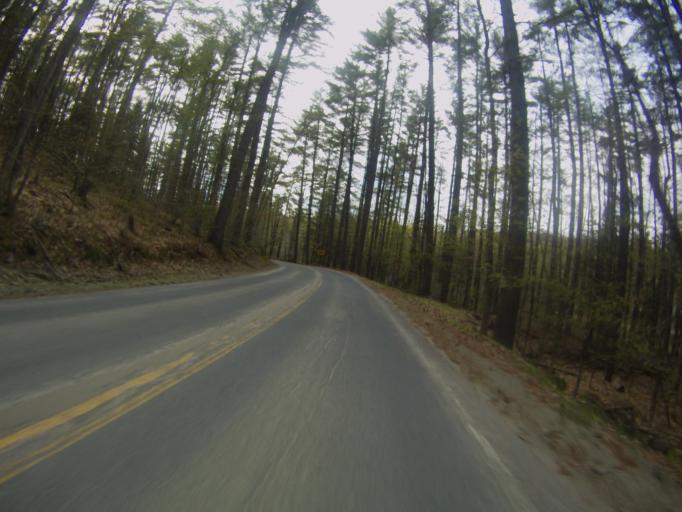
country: US
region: New York
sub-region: Warren County
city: Warrensburg
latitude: 43.8260
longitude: -73.9092
